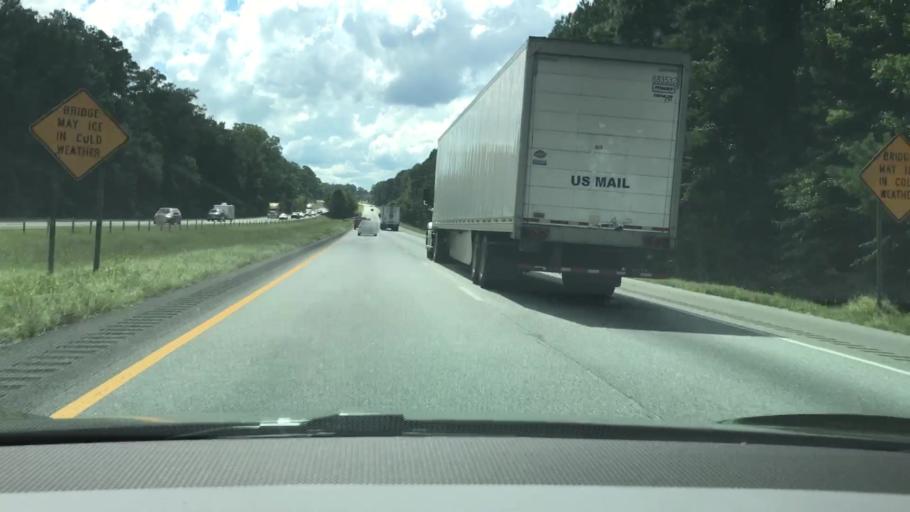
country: US
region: Alabama
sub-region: Macon County
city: Tuskegee
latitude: 32.5107
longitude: -85.5945
